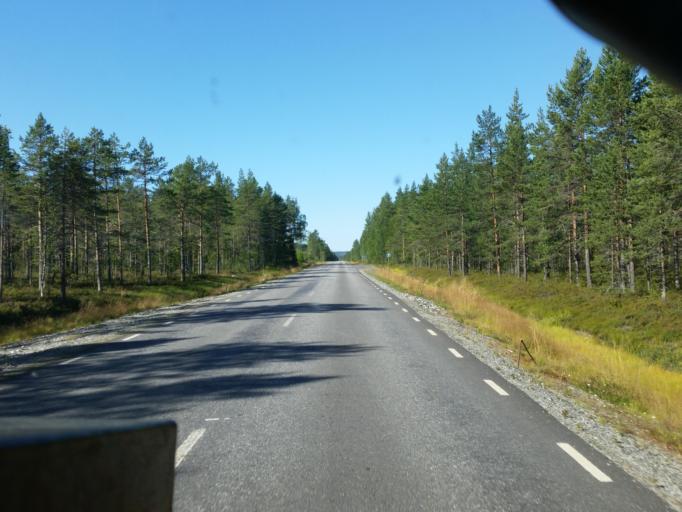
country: SE
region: Norrbotten
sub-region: Pitea Kommun
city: Roknas
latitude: 65.2018
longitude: 21.1664
